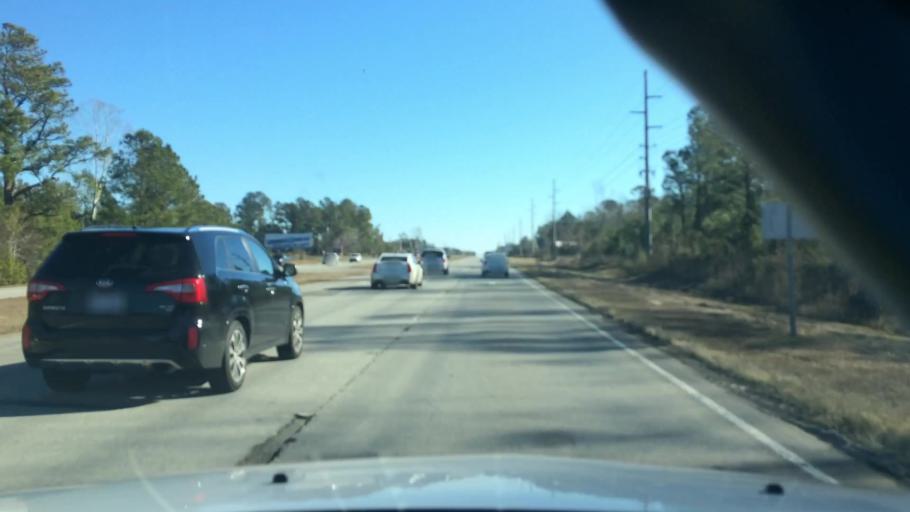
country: US
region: North Carolina
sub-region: Brunswick County
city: Sunset Beach
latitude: 33.9482
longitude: -78.4900
